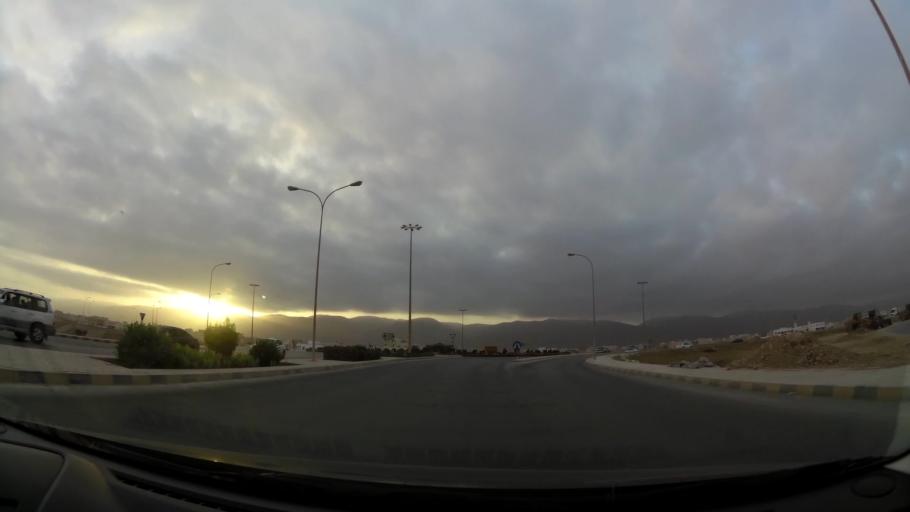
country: OM
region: Zufar
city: Salalah
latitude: 17.0306
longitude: 54.0298
